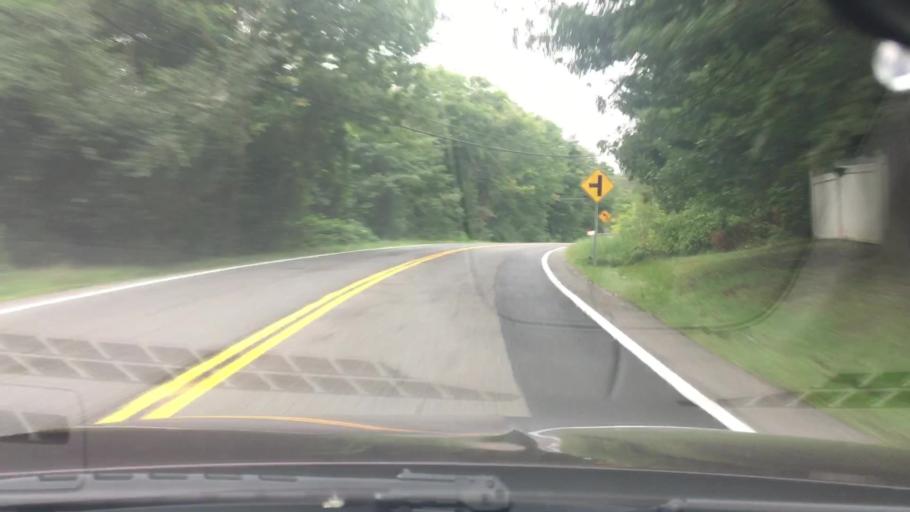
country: US
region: New York
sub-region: Dutchess County
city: Millbrook
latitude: 41.7936
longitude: -73.6973
